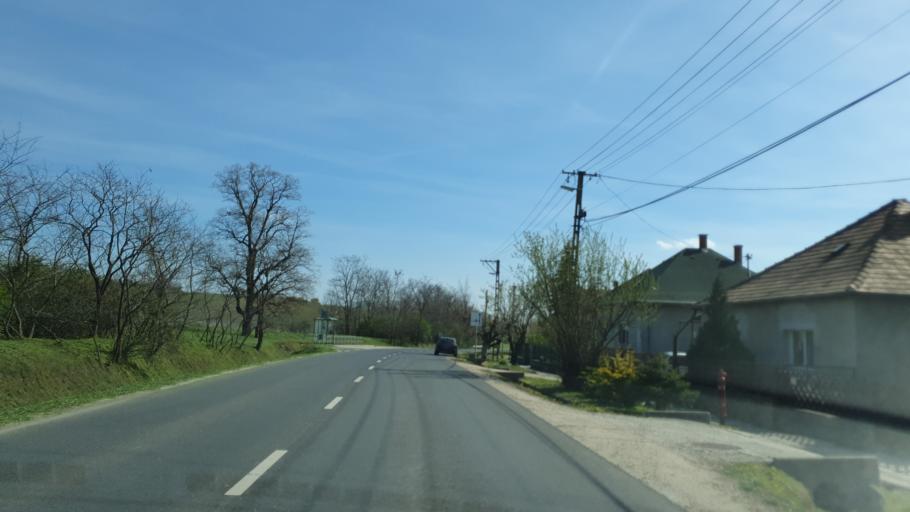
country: HU
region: Fejer
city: Mor
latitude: 47.3853
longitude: 18.2257
